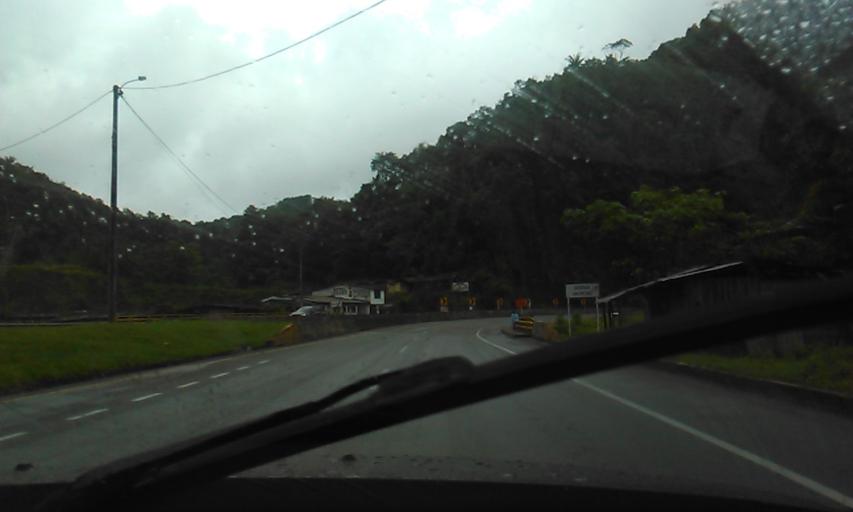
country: CO
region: Valle del Cauca
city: Buenaventura
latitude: 3.8652
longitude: -76.8291
